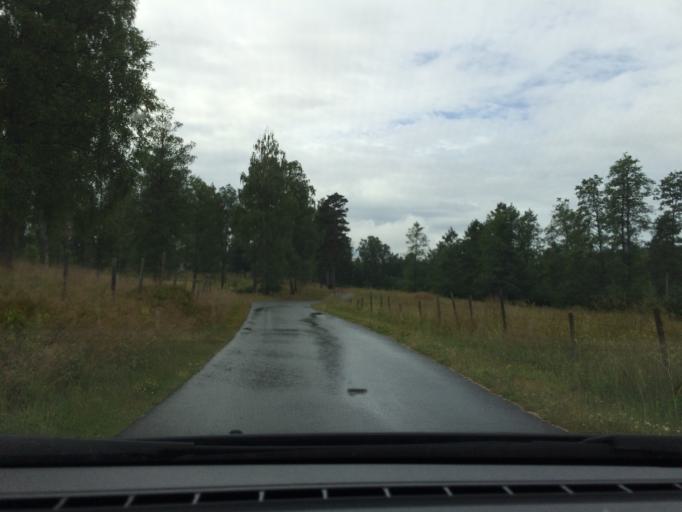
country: SE
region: Joenkoeping
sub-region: Varnamo Kommun
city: Varnamo
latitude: 57.1831
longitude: 13.9342
